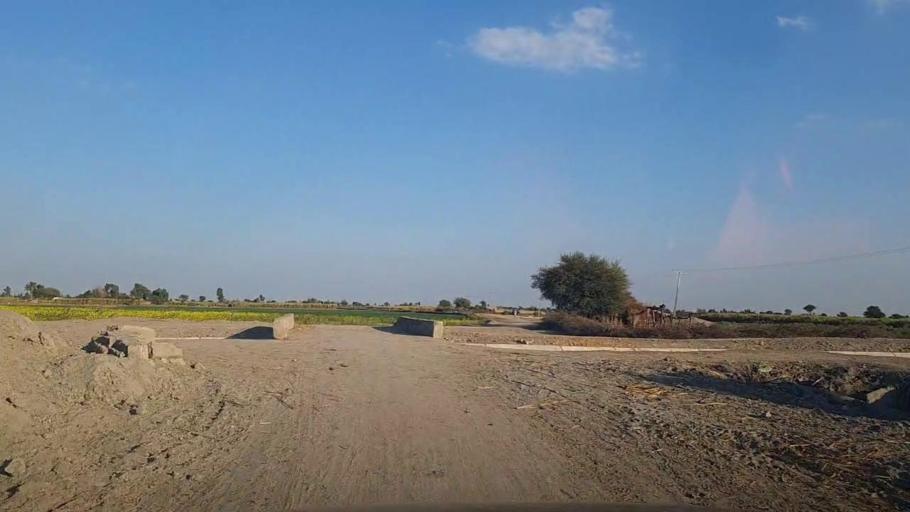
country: PK
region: Sindh
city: Jhol
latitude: 25.9195
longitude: 69.0408
